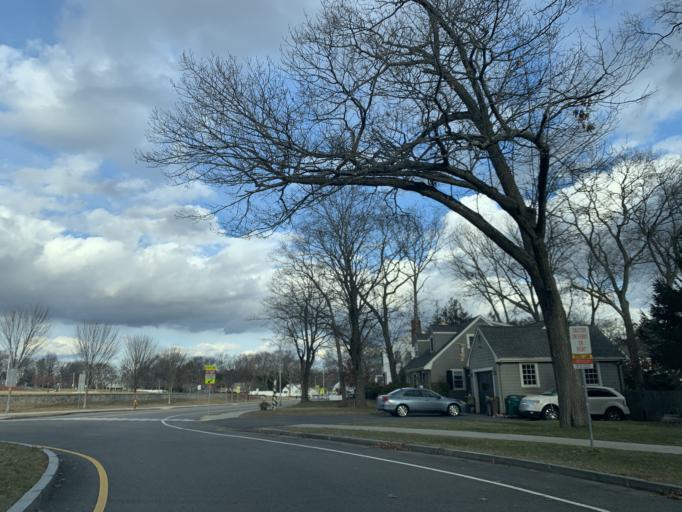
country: US
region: Massachusetts
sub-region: Norfolk County
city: Norwood
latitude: 42.1894
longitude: -71.2149
